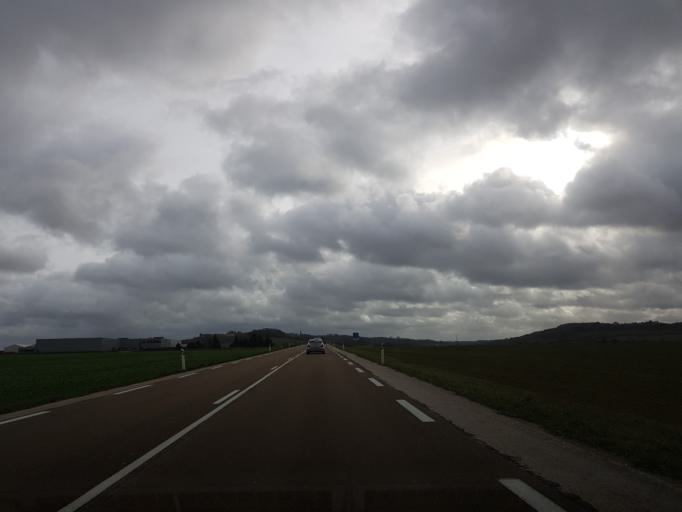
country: FR
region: Champagne-Ardenne
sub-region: Departement de la Haute-Marne
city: Langres
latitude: 47.8929
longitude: 5.3142
